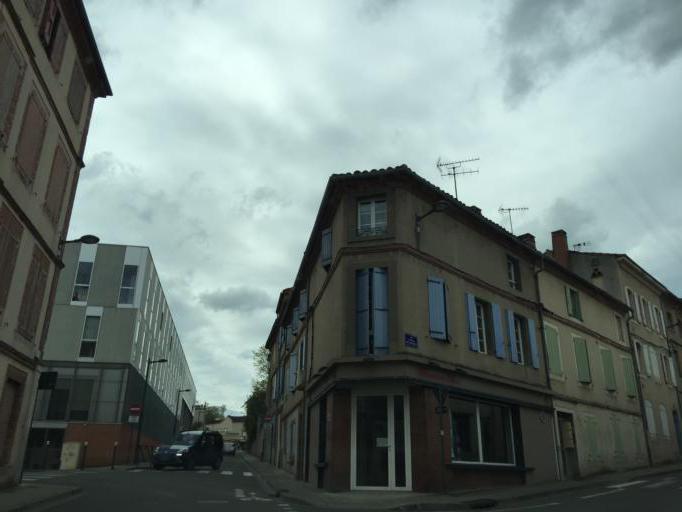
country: FR
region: Midi-Pyrenees
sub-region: Departement du Tarn
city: Albi
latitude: 43.9271
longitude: 2.1384
